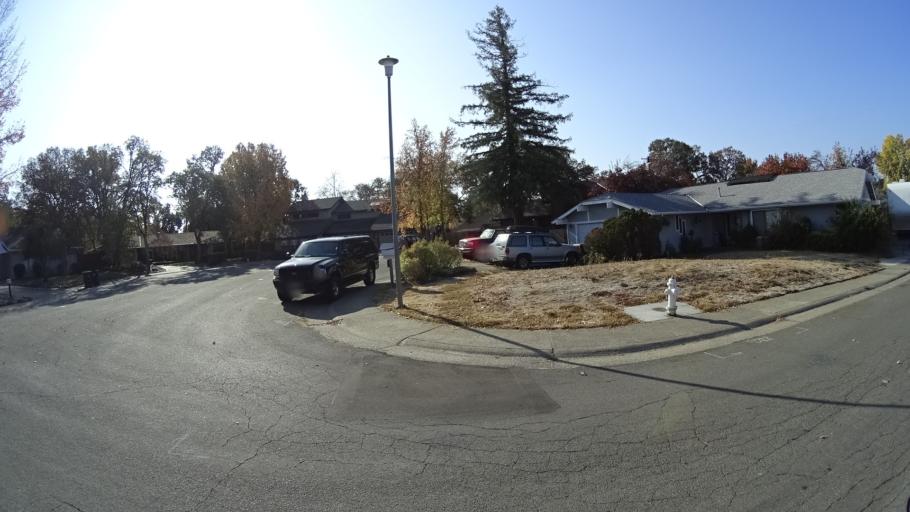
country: US
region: California
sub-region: Sacramento County
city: Citrus Heights
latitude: 38.7144
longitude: -121.2644
